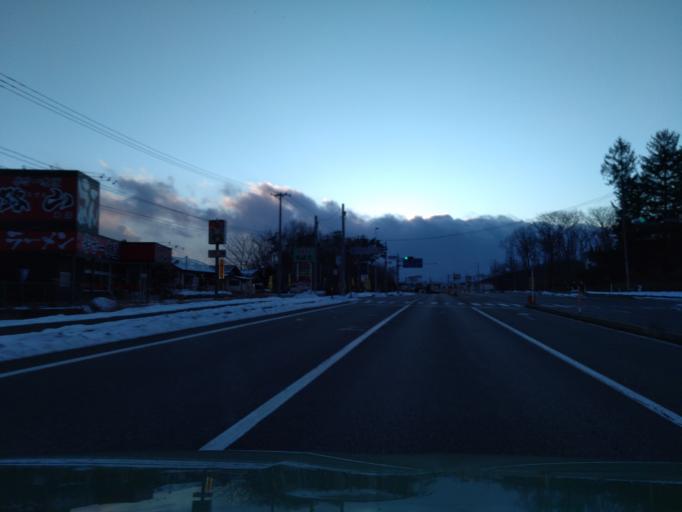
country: JP
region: Iwate
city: Shizukuishi
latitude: 39.6996
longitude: 141.0263
